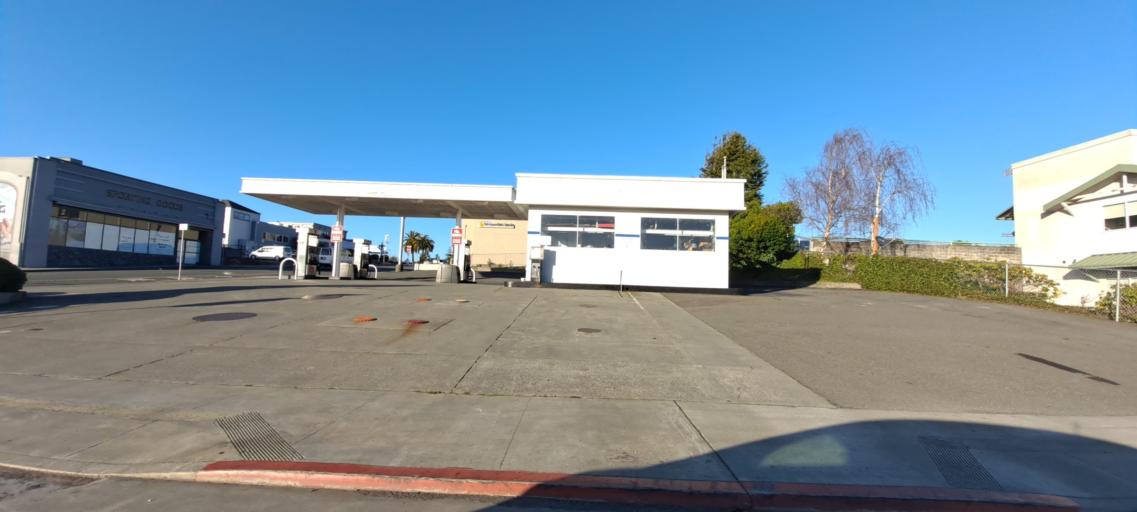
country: US
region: California
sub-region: Humboldt County
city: Arcata
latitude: 40.8672
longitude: -124.0861
